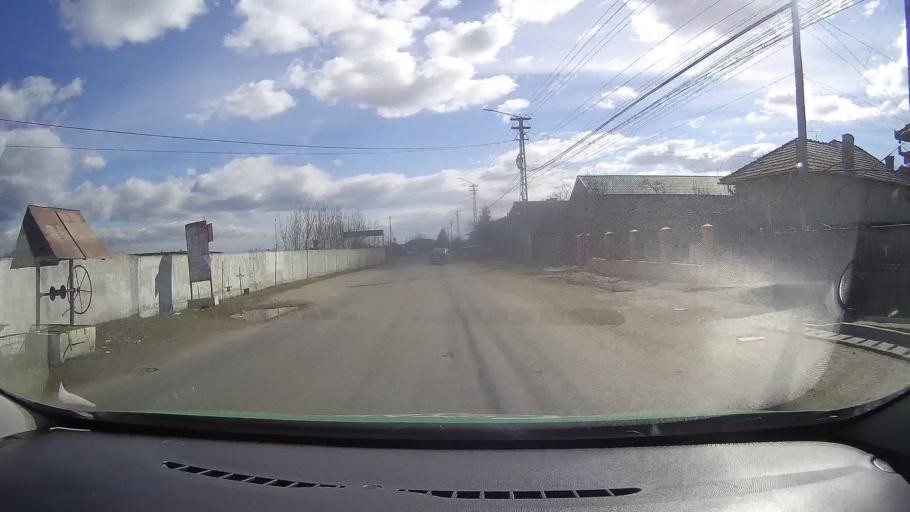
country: RO
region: Dambovita
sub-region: Comuna Doicesti
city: Doicesti
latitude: 44.9862
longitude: 25.3845
